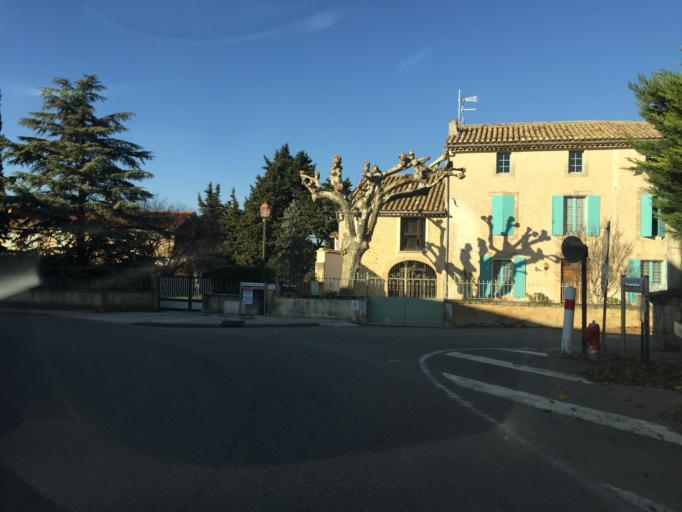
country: FR
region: Provence-Alpes-Cote d'Azur
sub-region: Departement du Vaucluse
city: Sainte-Cecile-les-Vignes
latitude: 44.2453
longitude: 4.8926
